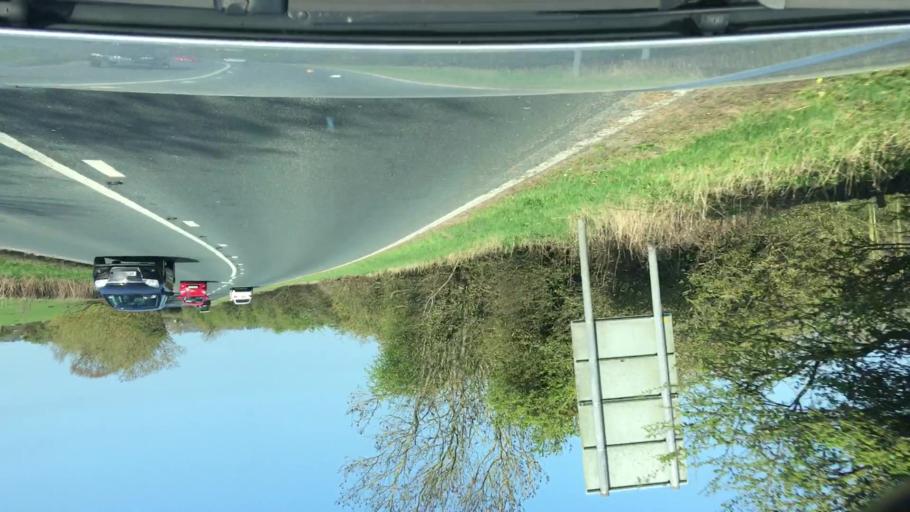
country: GB
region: England
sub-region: North Yorkshire
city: Pannal
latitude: 53.9414
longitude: -1.5376
